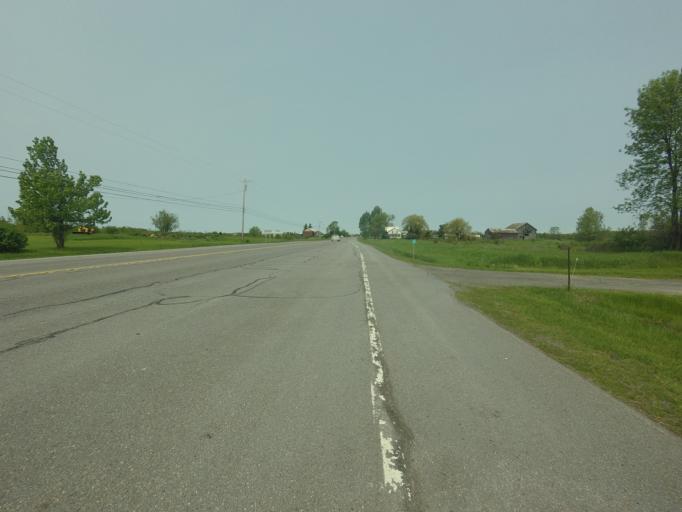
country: US
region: New York
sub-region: Jefferson County
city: Dexter
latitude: 44.0444
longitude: -76.0861
